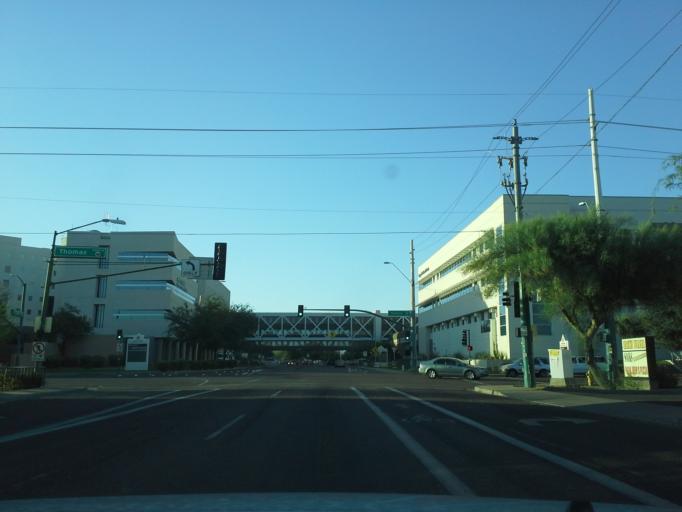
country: US
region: Arizona
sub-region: Maricopa County
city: Phoenix
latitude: 33.4798
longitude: -112.0783
